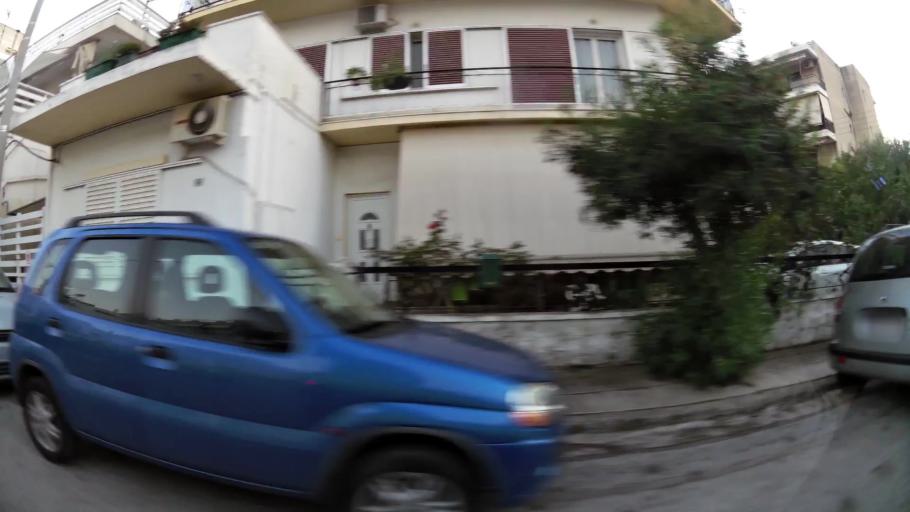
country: GR
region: Attica
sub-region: Nomarchia Athinas
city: Argyroupoli
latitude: 37.8893
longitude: 23.7515
